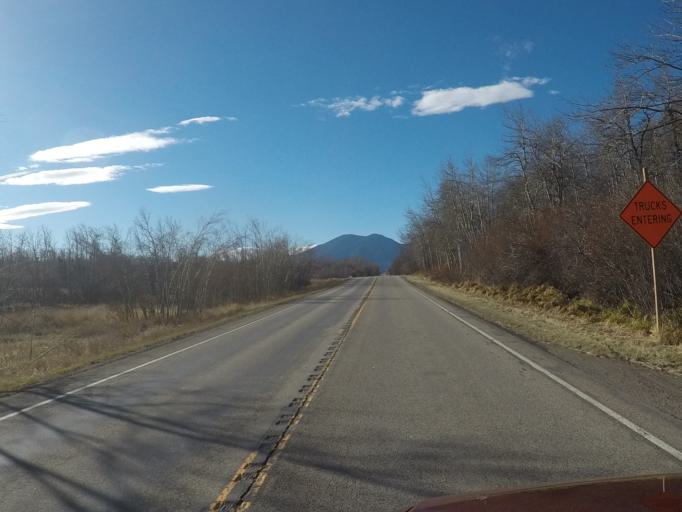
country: US
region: Montana
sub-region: Carbon County
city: Red Lodge
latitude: 45.2285
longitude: -109.2390
